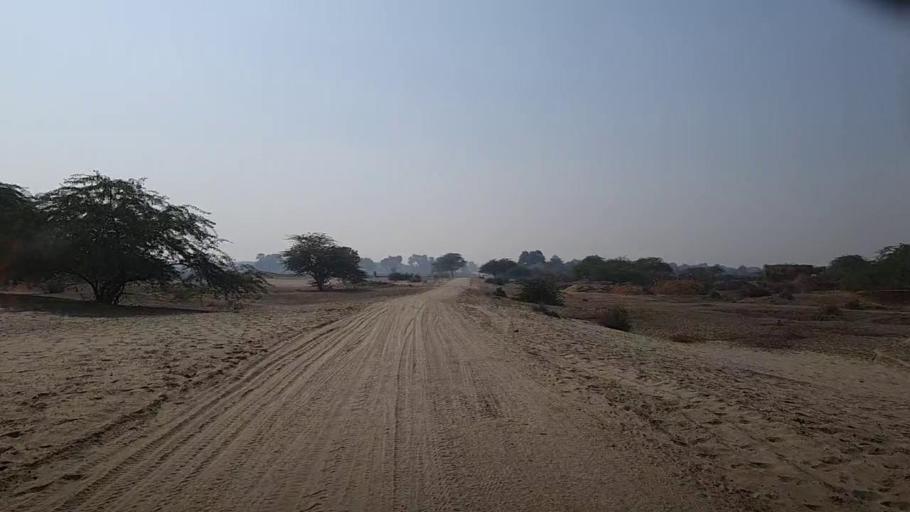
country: PK
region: Sindh
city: Bozdar
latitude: 27.2177
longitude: 68.5810
